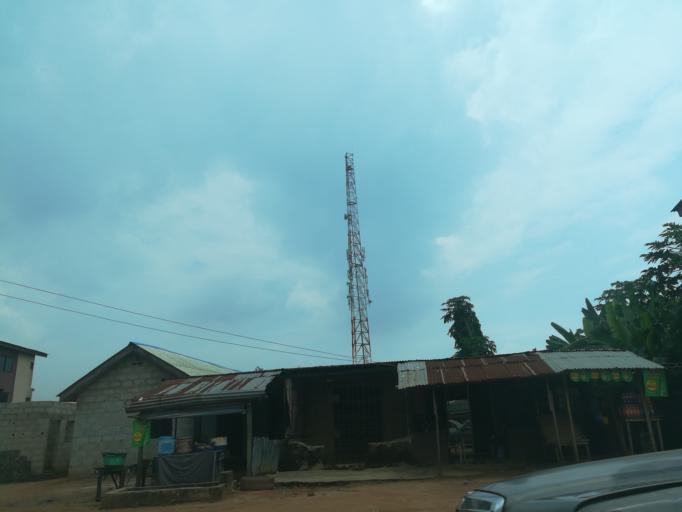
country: NG
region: Lagos
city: Ikorodu
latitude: 6.5671
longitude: 3.5916
